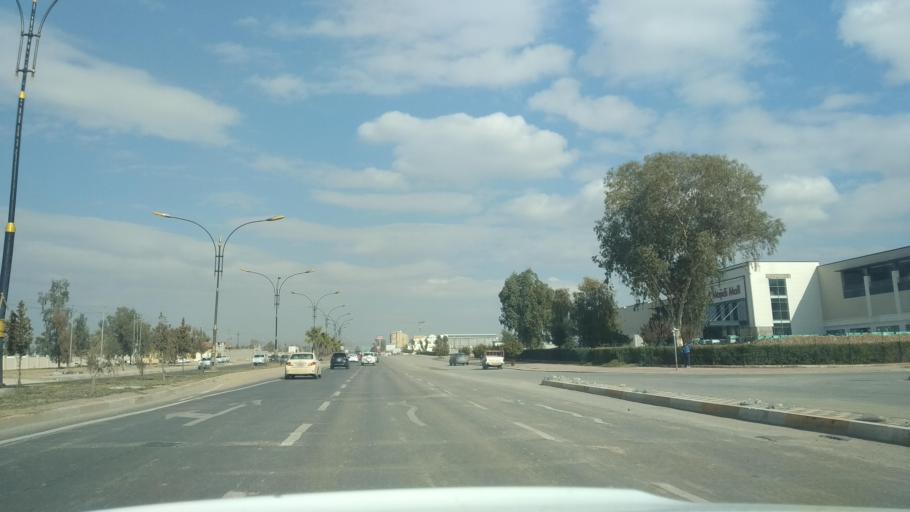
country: IQ
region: Arbil
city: Erbil
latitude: 36.2530
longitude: 44.0789
